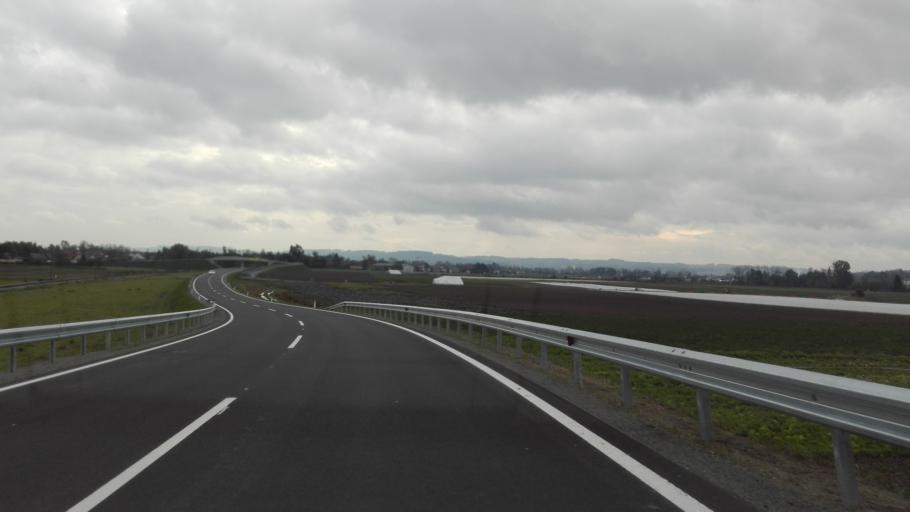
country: AT
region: Upper Austria
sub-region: Politischer Bezirk Urfahr-Umgebung
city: Feldkirchen an der Donau
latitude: 48.3296
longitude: 14.0048
